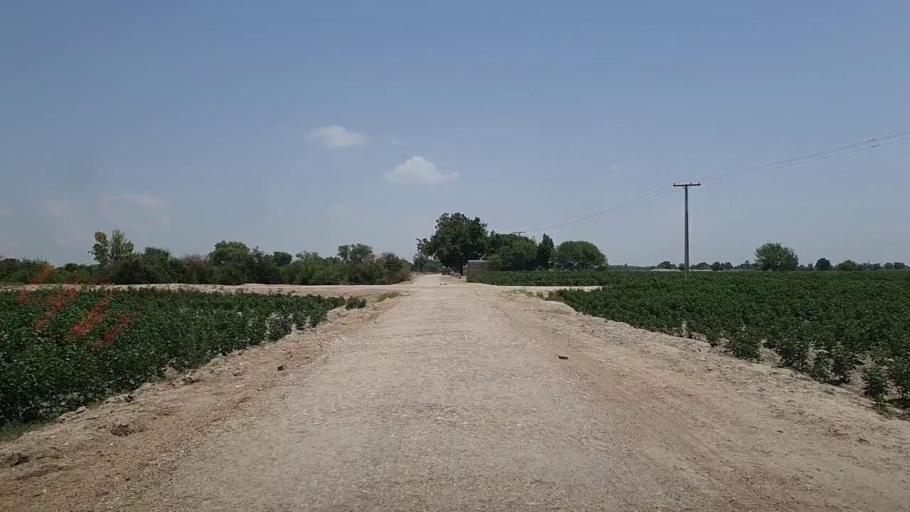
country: PK
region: Sindh
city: Pad Idan
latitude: 26.7530
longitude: 68.3000
